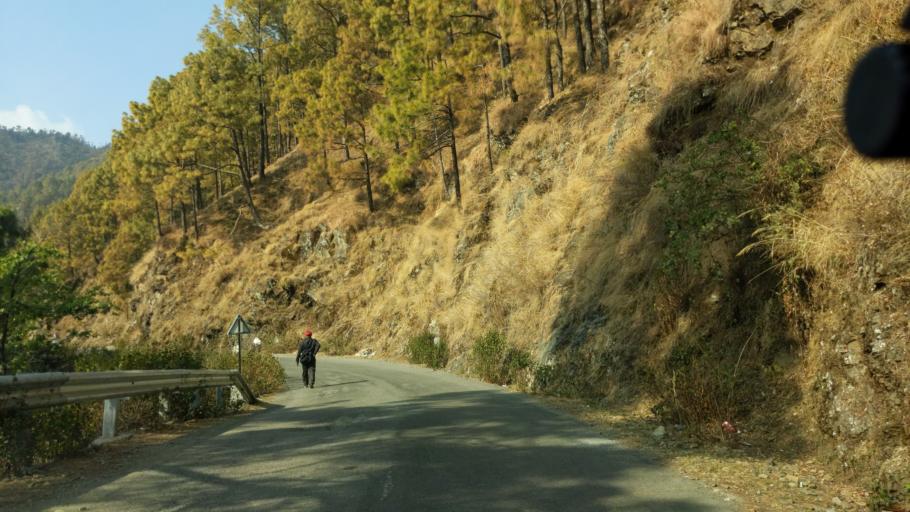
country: IN
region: Uttarakhand
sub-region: Naini Tal
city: Bhowali
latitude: 29.3892
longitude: 79.5381
